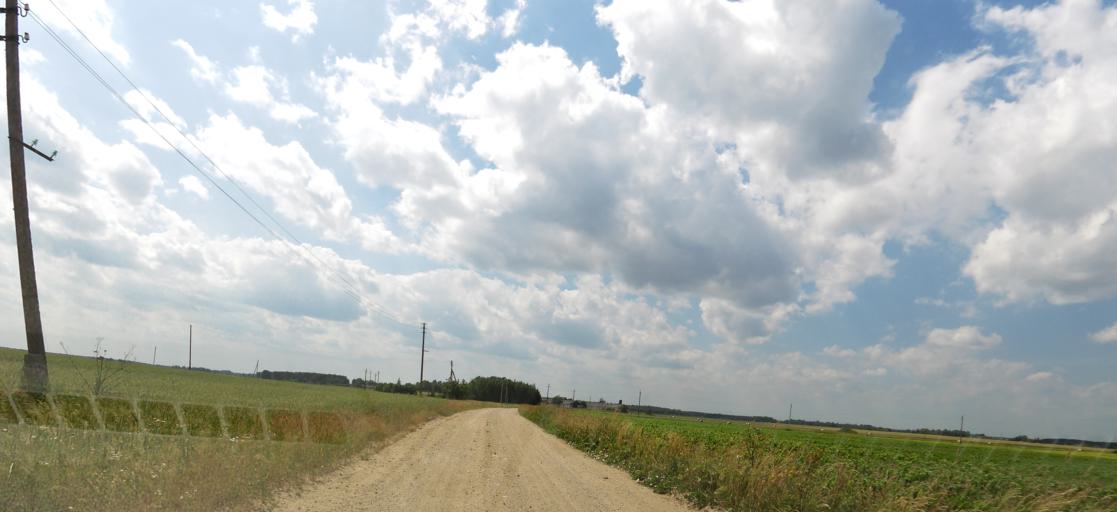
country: LT
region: Panevezys
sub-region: Birzai
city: Birzai
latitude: 56.1204
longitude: 24.8938
